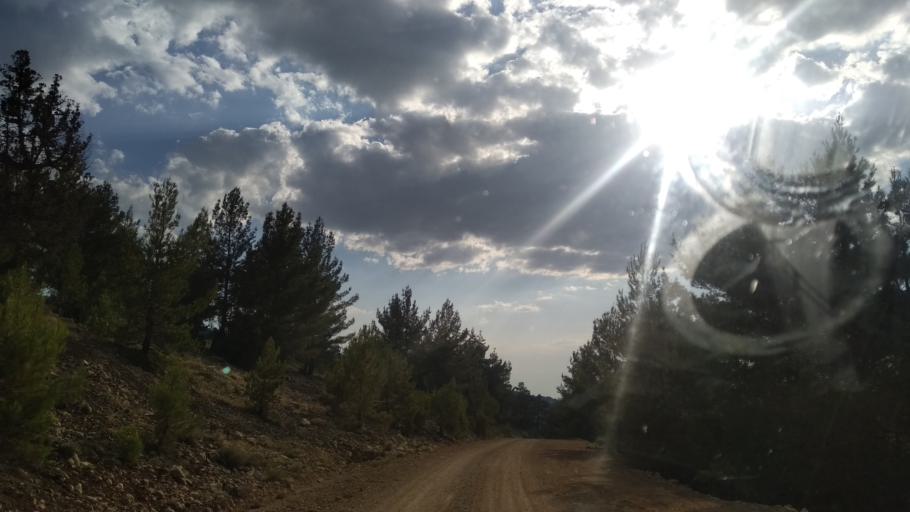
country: TR
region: Mersin
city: Sarikavak
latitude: 36.6006
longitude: 33.7184
